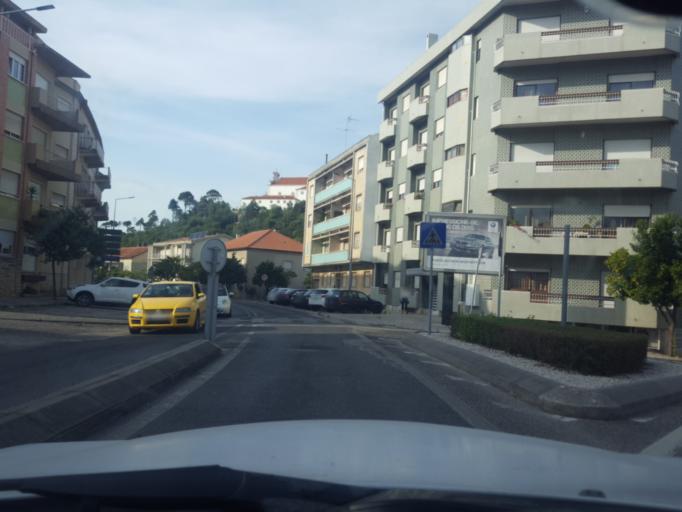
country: PT
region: Leiria
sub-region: Leiria
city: Leiria
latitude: 39.7360
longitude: -8.7992
